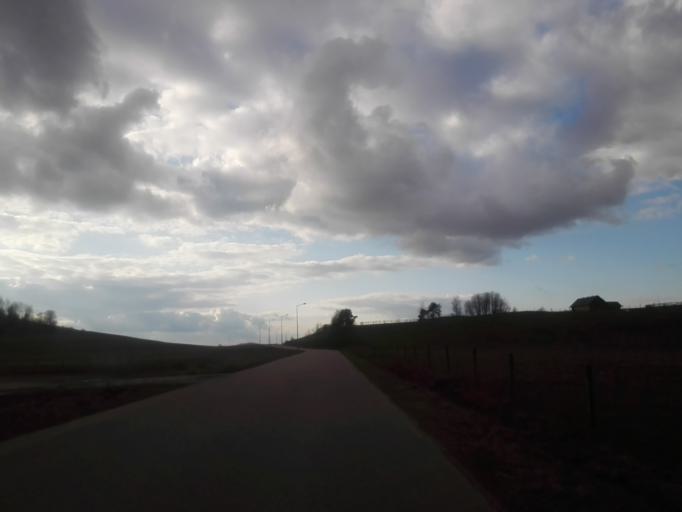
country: PL
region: Podlasie
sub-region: Suwalki
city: Suwalki
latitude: 54.2061
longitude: 22.9811
